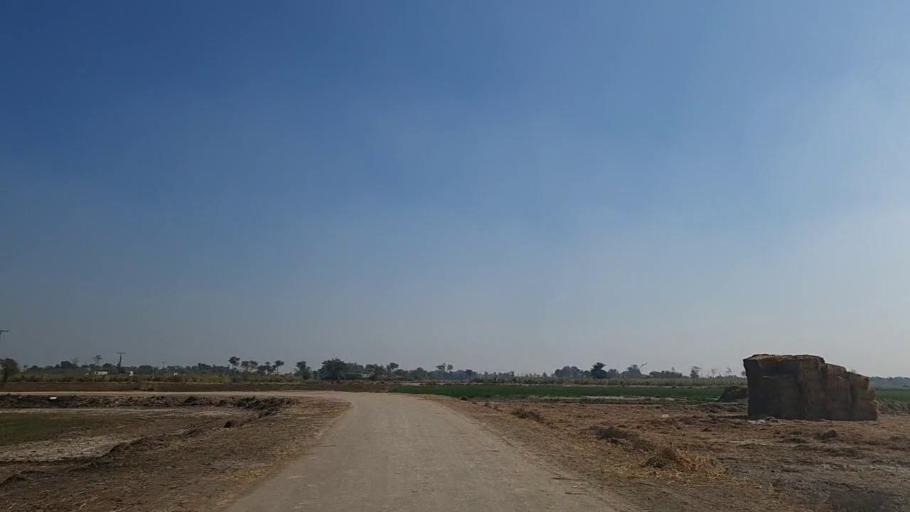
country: PK
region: Sindh
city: Daur
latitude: 26.4811
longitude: 68.3236
